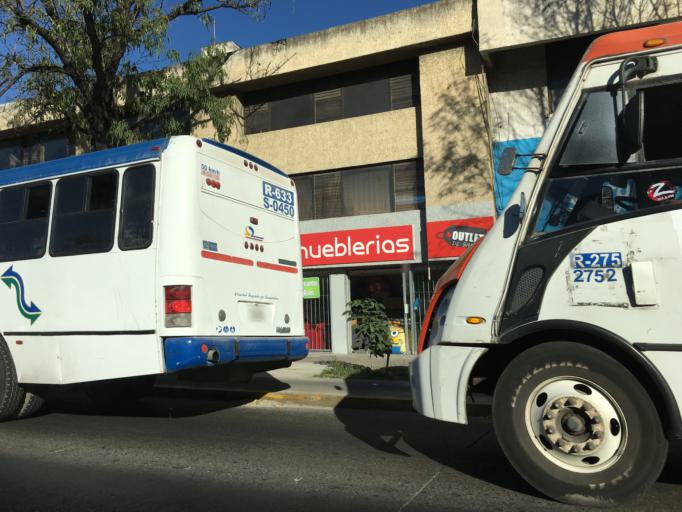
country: MX
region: Jalisco
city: Guadalajara
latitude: 20.6809
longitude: -103.3540
